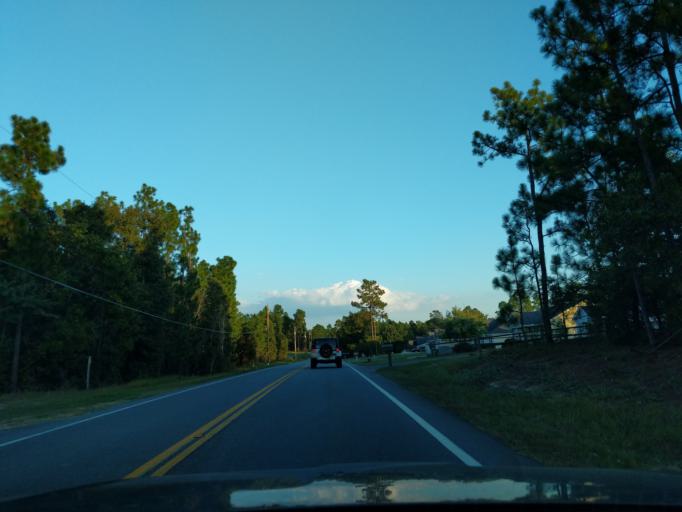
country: US
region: South Carolina
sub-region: Aiken County
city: Burnettown
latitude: 33.5382
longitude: -81.8668
